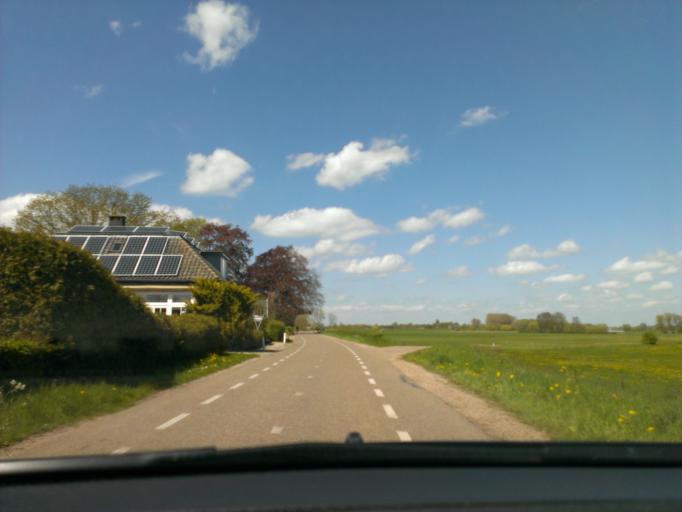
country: NL
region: Overijssel
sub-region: Gemeente Olst-Wijhe
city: Olst
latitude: 52.3106
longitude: 6.0913
